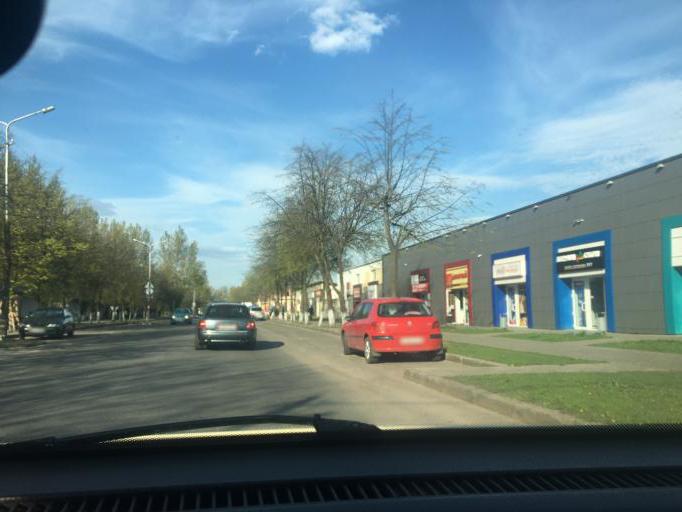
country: BY
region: Mogilev
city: Babruysk
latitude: 53.1625
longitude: 29.2045
